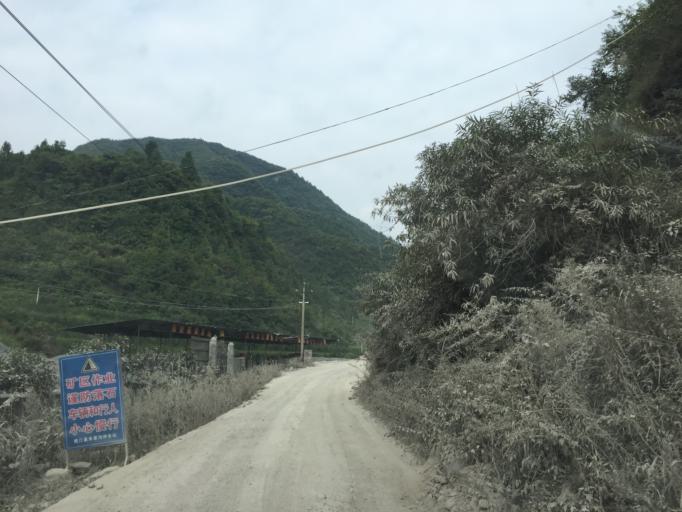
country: CN
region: Guizhou Sheng
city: Longquan
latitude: 28.1951
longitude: 108.0466
